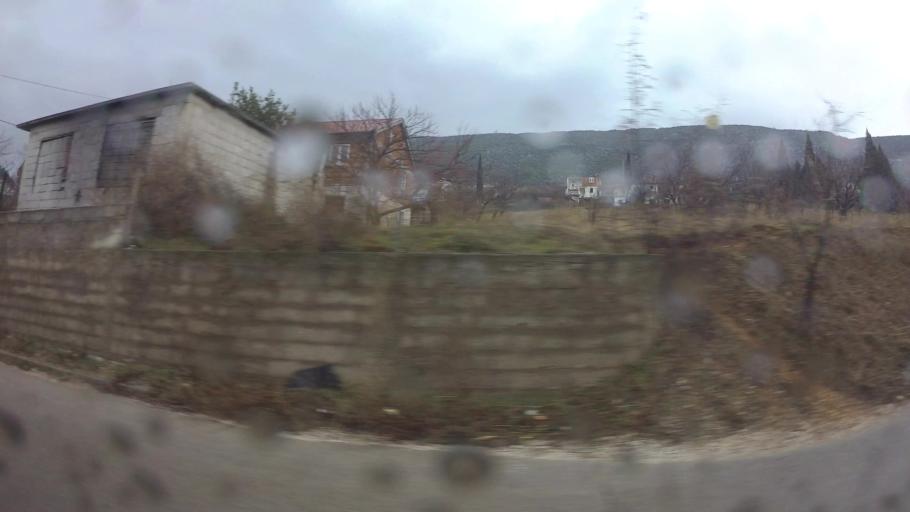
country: BA
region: Federation of Bosnia and Herzegovina
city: Rodoc
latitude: 43.3039
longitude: 17.8519
